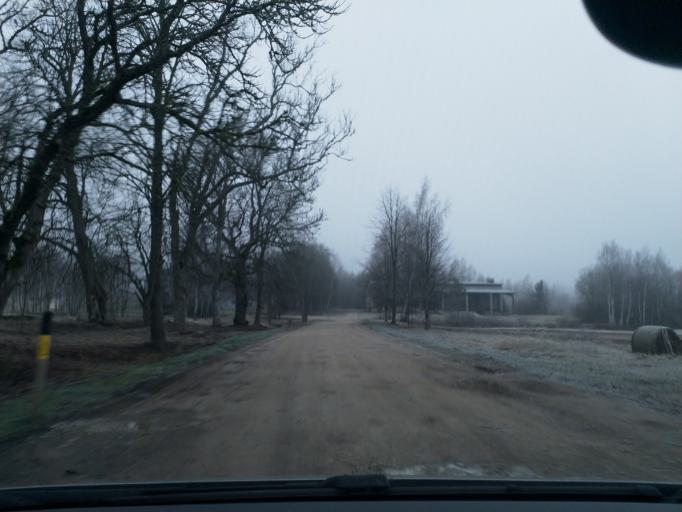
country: LV
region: Kuldigas Rajons
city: Kuldiga
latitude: 56.8413
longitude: 21.9426
